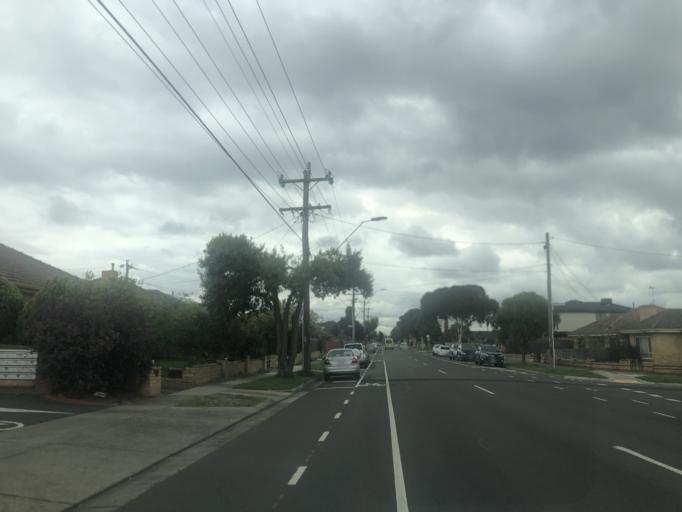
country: AU
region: Victoria
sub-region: Greater Dandenong
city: Dandenong North
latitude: -37.9739
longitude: 145.2103
